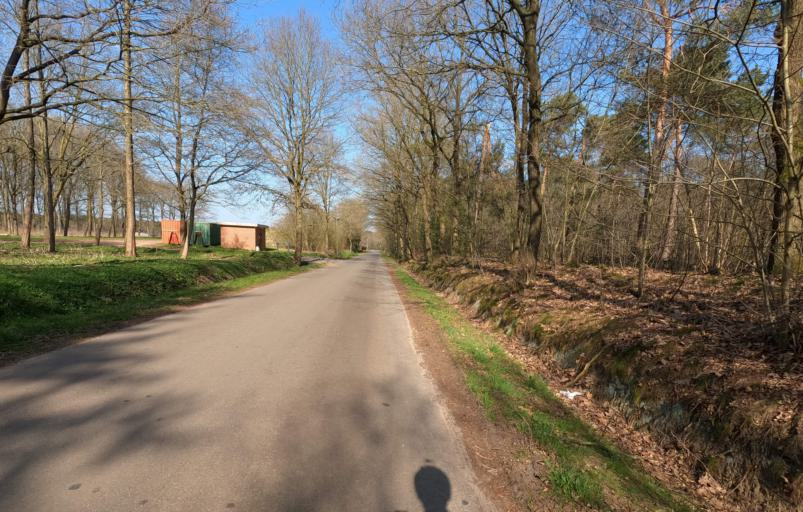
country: BE
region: Flanders
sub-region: Provincie Antwerpen
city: Merksplas
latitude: 51.3812
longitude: 4.8658
